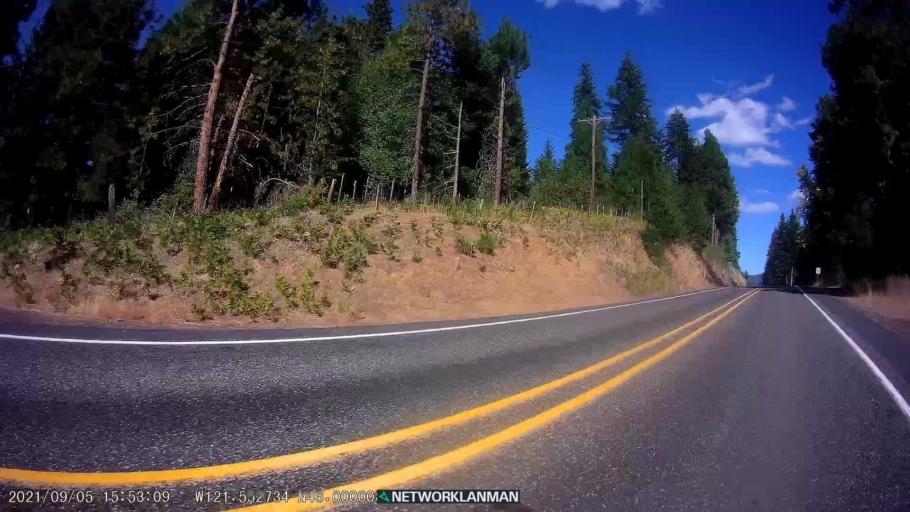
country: US
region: Washington
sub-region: Klickitat County
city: White Salmon
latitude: 46.0000
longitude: -121.5524
